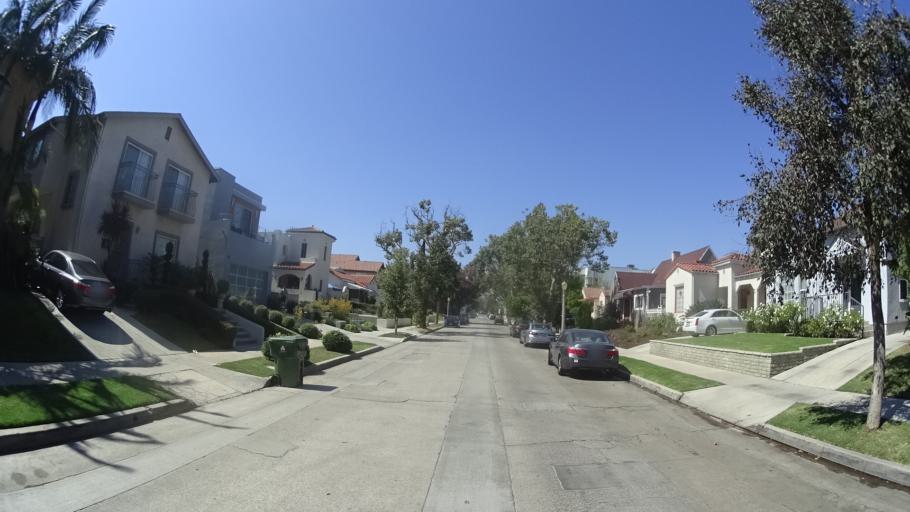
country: US
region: California
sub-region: Los Angeles County
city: Hollywood
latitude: 34.0807
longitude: -118.3397
